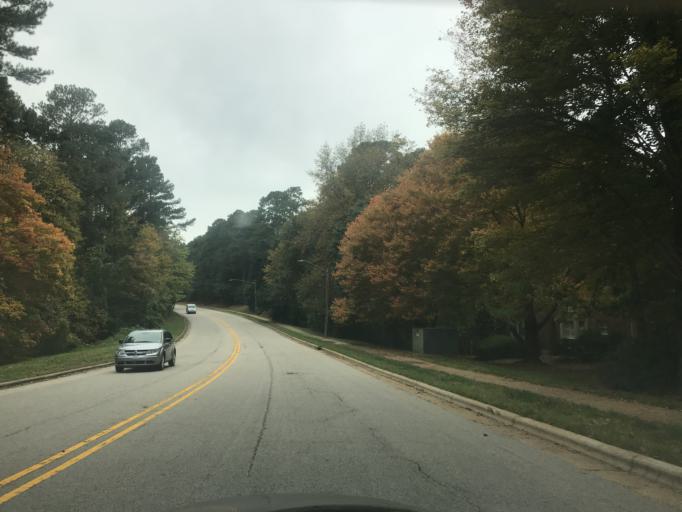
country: US
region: North Carolina
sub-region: Wake County
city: West Raleigh
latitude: 35.8845
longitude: -78.6708
